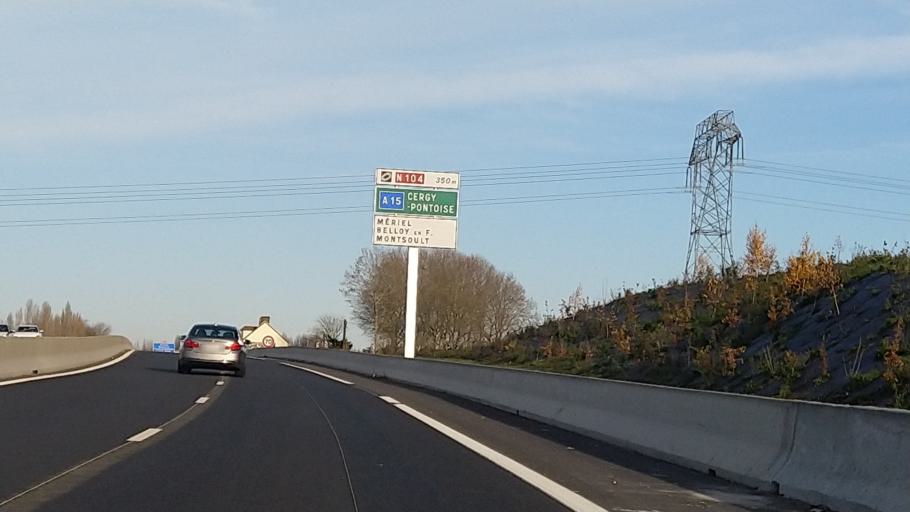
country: FR
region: Ile-de-France
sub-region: Departement du Val-d'Oise
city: Moisselles
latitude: 49.0590
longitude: 2.3318
